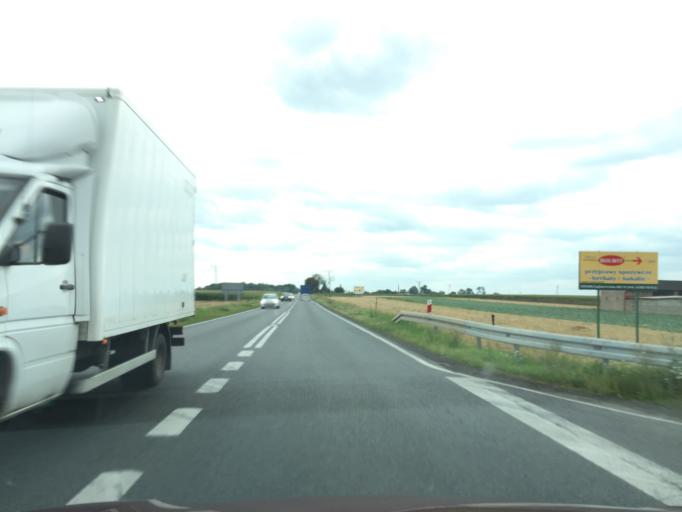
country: PL
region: Greater Poland Voivodeship
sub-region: Kalisz
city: Kalisz
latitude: 51.8239
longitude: 18.0940
